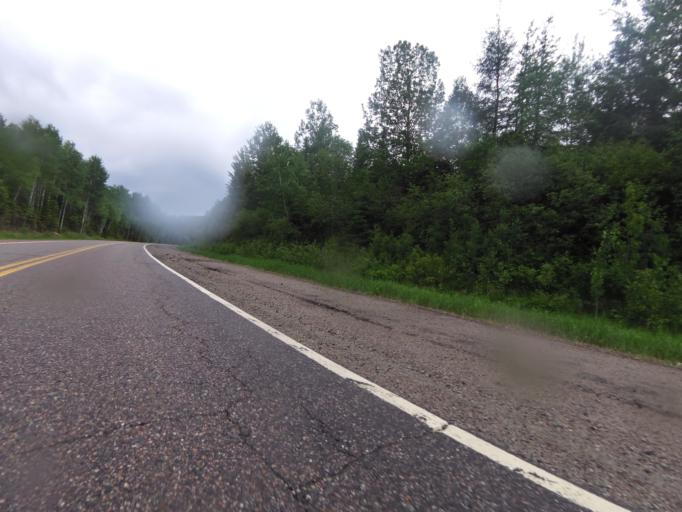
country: CA
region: Quebec
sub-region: Outaouais
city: Shawville
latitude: 45.9139
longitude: -76.2568
